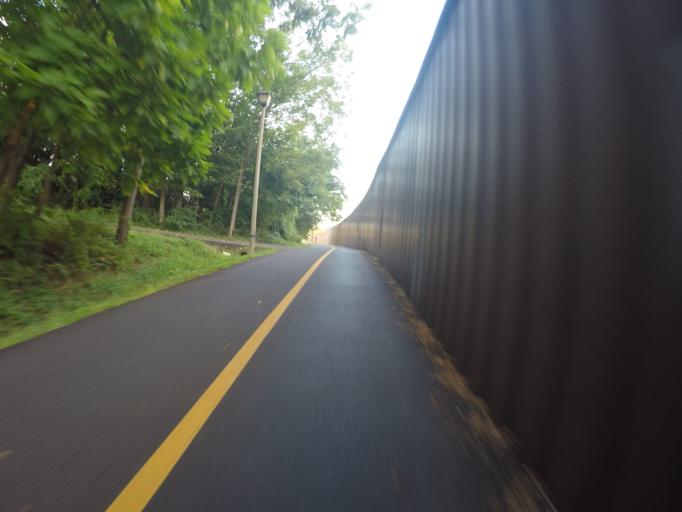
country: US
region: Virginia
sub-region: Arlington County
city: Arlington
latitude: 38.8800
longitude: -77.1272
